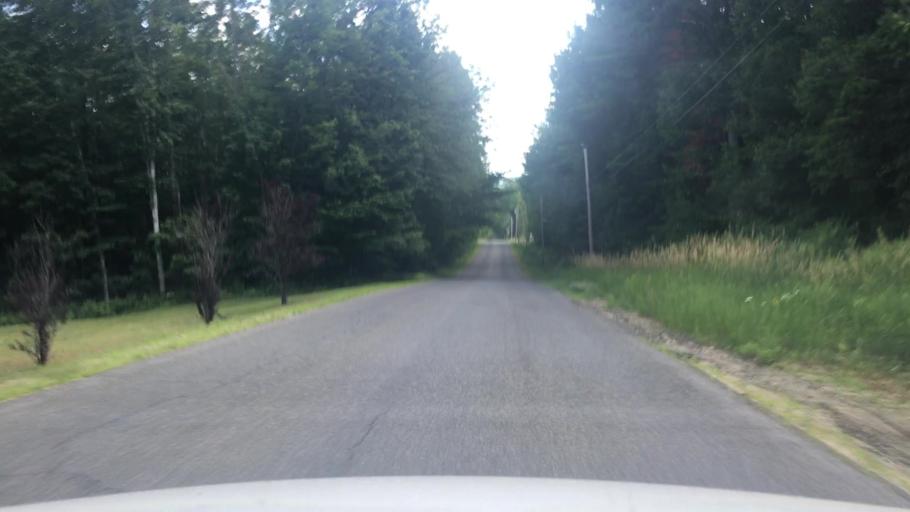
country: US
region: Maine
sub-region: Franklin County
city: Wilton
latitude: 44.6233
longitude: -70.2320
